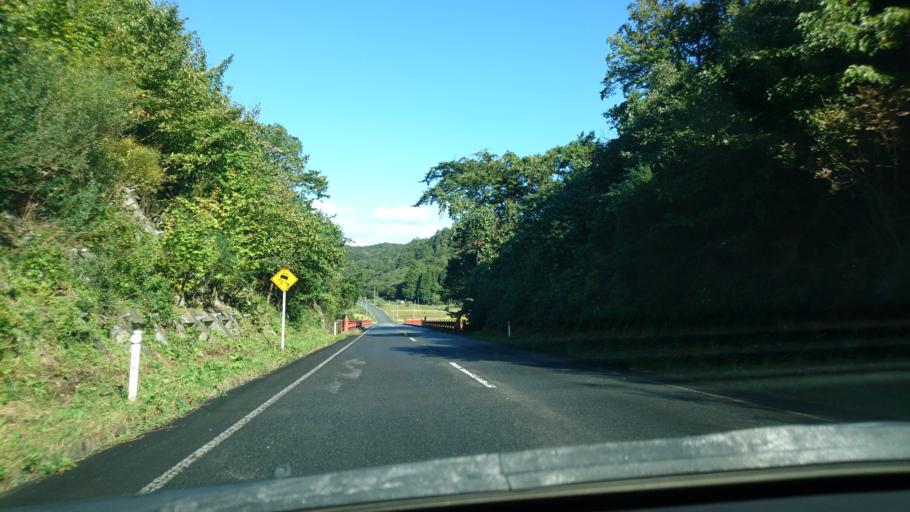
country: JP
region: Iwate
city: Ichinoseki
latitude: 39.0176
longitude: 141.0238
